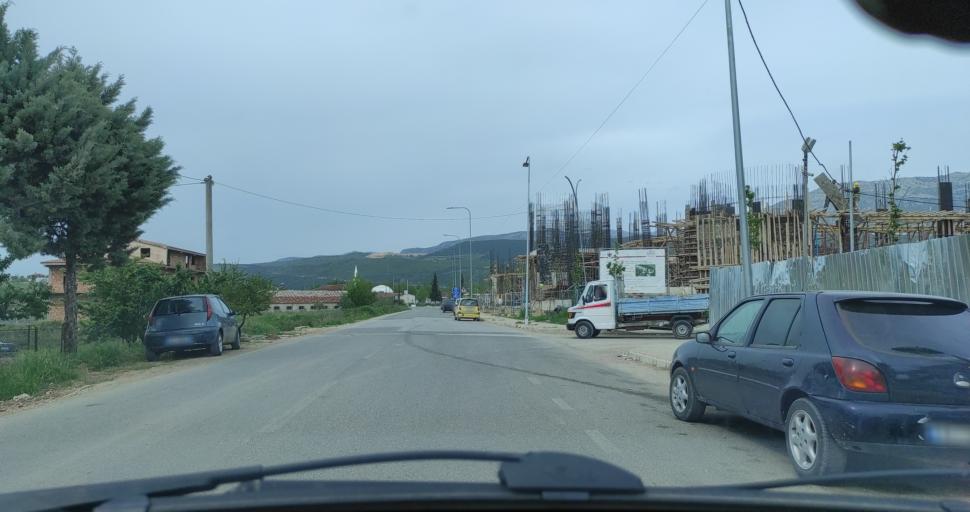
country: AL
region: Durres
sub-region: Rrethi i Krujes
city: Fushe-Kruje
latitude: 41.4854
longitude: 19.7252
